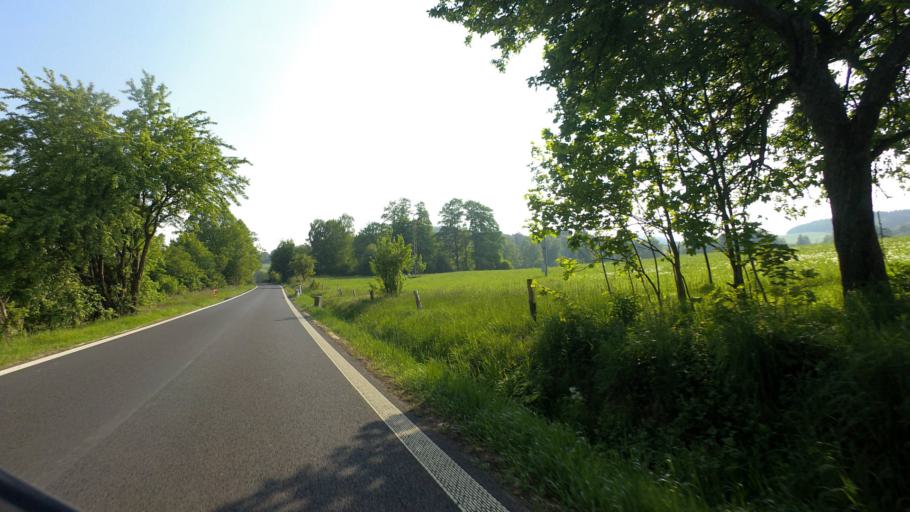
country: CZ
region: Ustecky
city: Dolni Poustevna
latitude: 51.0099
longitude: 14.2995
